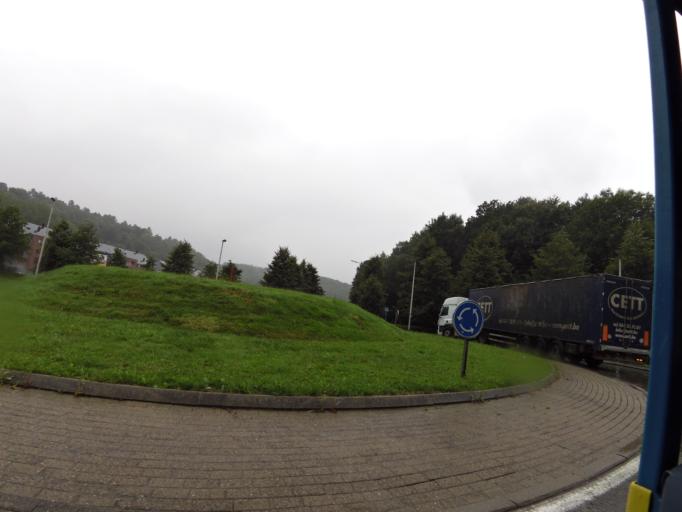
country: BE
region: Wallonia
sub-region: Province de Namur
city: Rochefort
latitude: 50.1596
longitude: 5.2449
